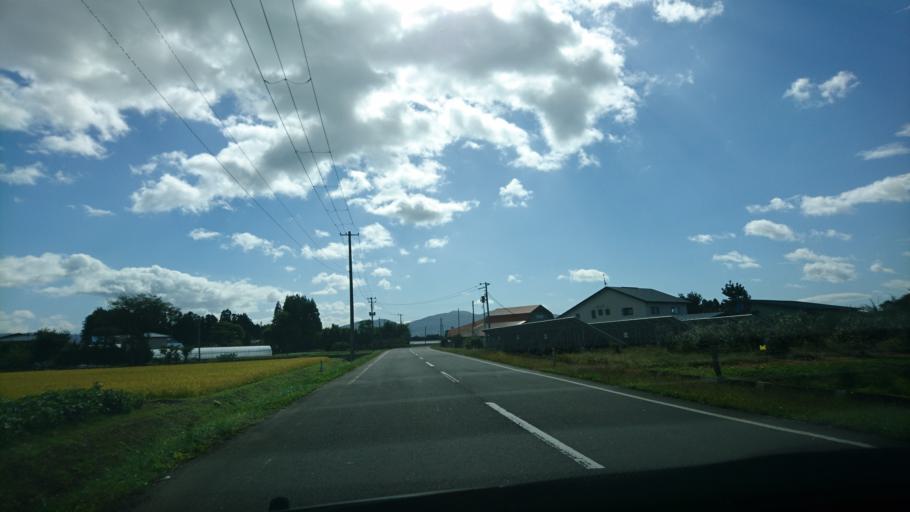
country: JP
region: Iwate
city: Mizusawa
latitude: 39.0783
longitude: 141.1063
